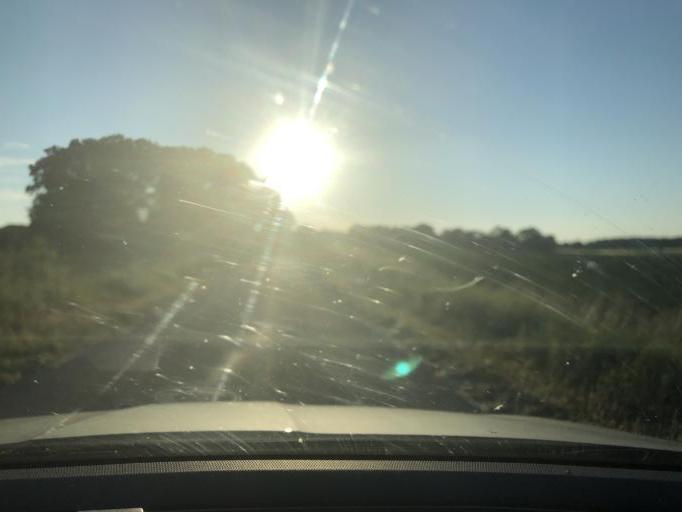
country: SE
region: Blekinge
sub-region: Karlshamns Kommun
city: Morrum
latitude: 56.1405
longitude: 14.6542
